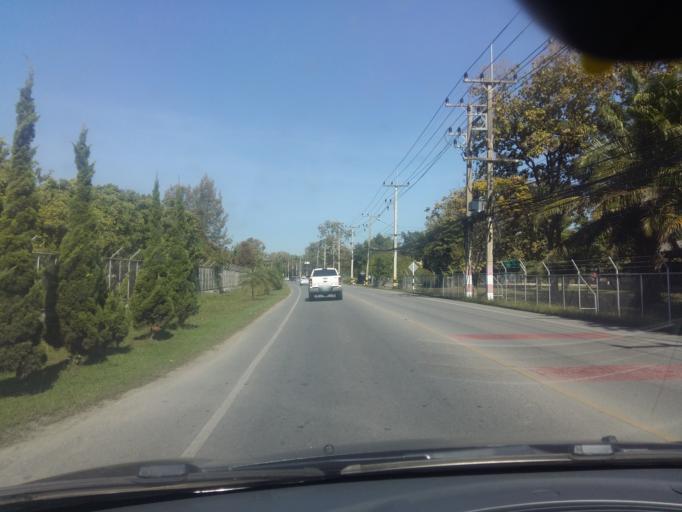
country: TH
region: Chiang Mai
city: Chiang Mai
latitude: 18.7785
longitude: 98.9669
